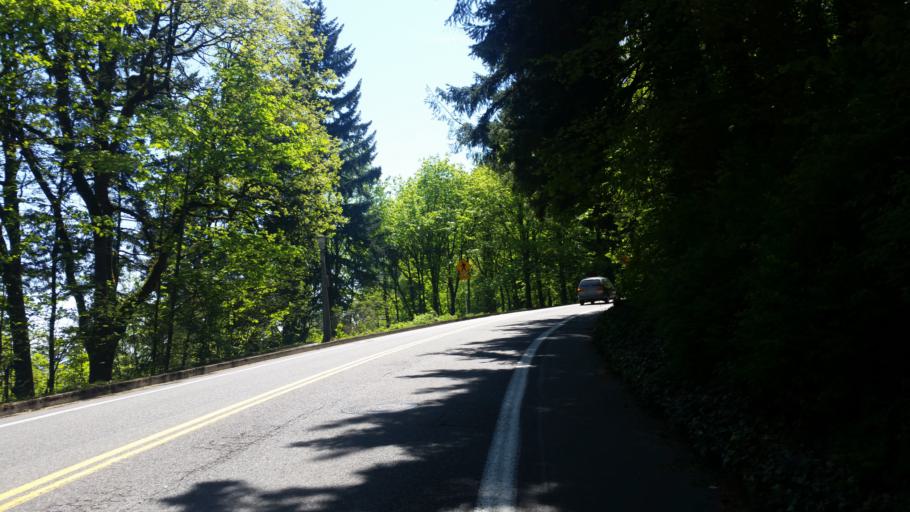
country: US
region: Oregon
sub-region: Multnomah County
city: Portland
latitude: 45.4969
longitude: -122.6805
